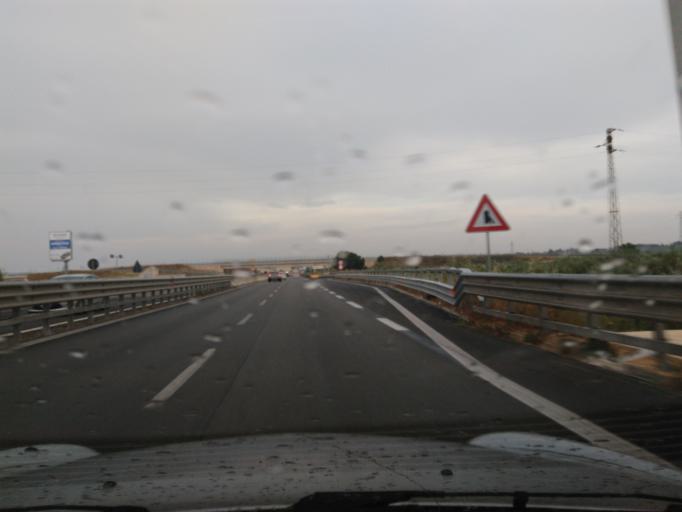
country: IT
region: Apulia
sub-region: Provincia di Bari
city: Molfetta
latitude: 41.2035
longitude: 16.5689
